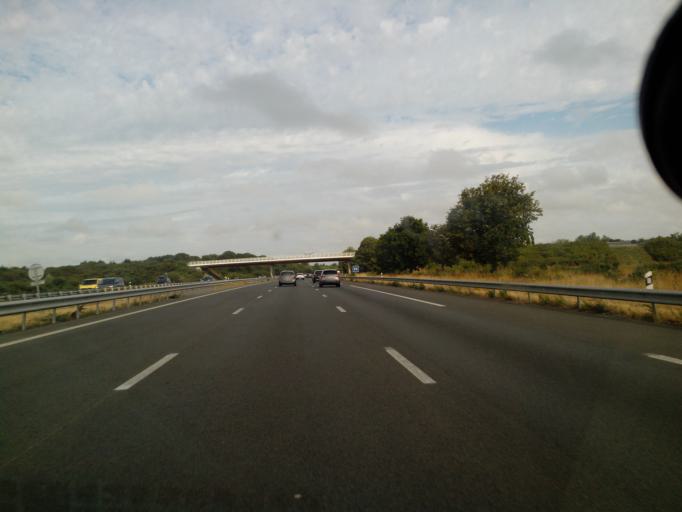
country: FR
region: Pays de la Loire
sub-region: Departement de la Loire-Atlantique
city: Malville
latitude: 47.3548
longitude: -1.8888
